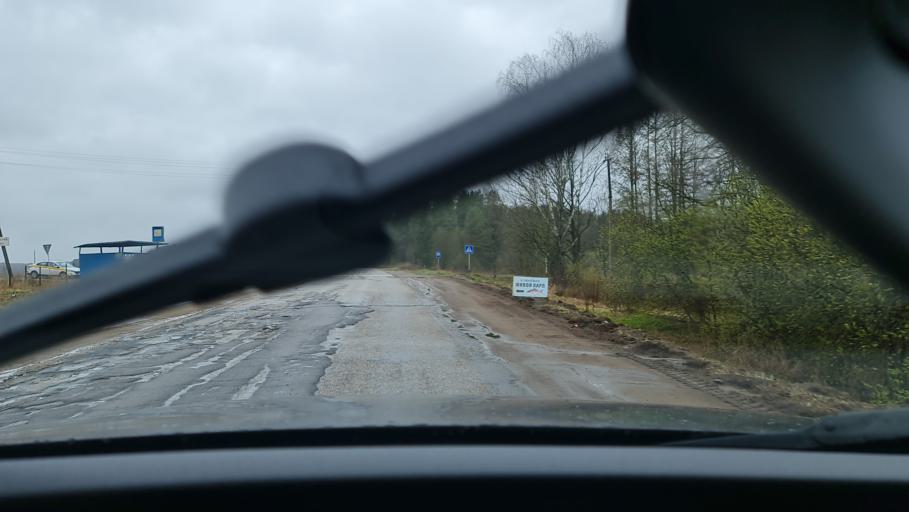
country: RU
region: Novgorod
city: Valday
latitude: 58.0395
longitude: 32.9291
